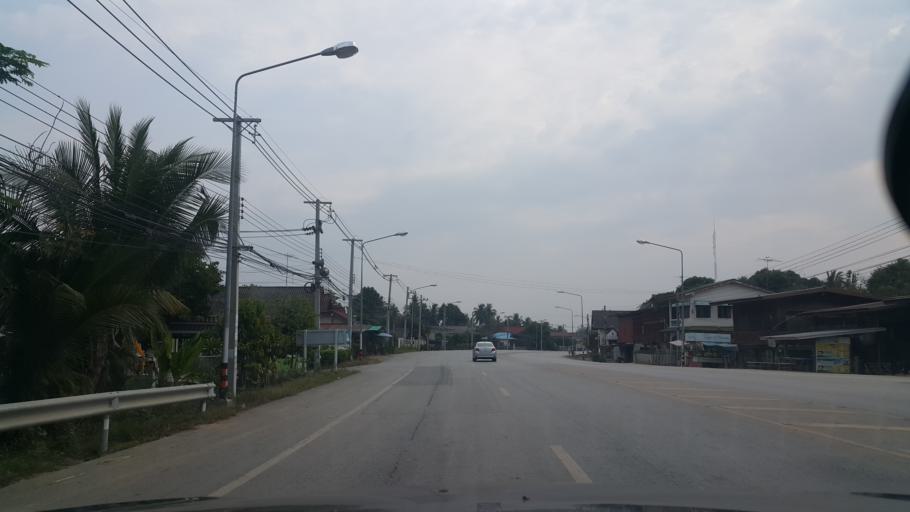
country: TH
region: Sukhothai
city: Si Samrong
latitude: 17.1610
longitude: 99.8663
